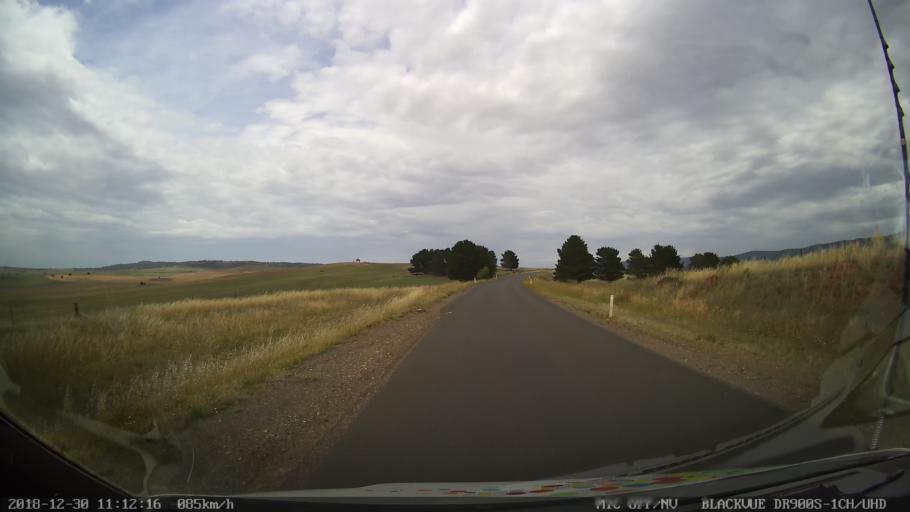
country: AU
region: New South Wales
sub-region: Snowy River
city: Jindabyne
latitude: -36.5268
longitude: 148.7585
